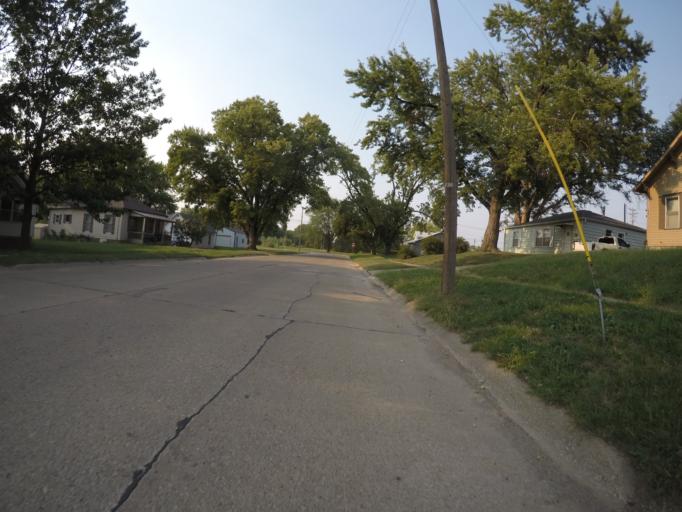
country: US
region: Nebraska
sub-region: Gage County
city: Beatrice
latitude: 40.2765
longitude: -96.7480
